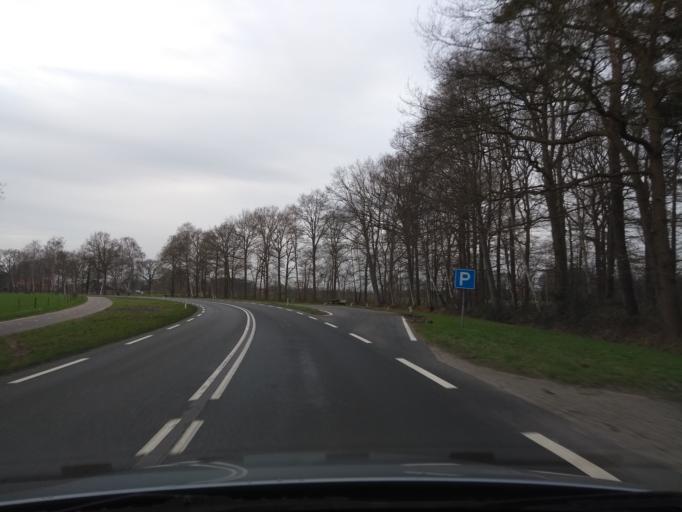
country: NL
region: Overijssel
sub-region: Gemeente Hof van Twente
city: Hengevelde
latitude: 52.2209
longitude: 6.6694
